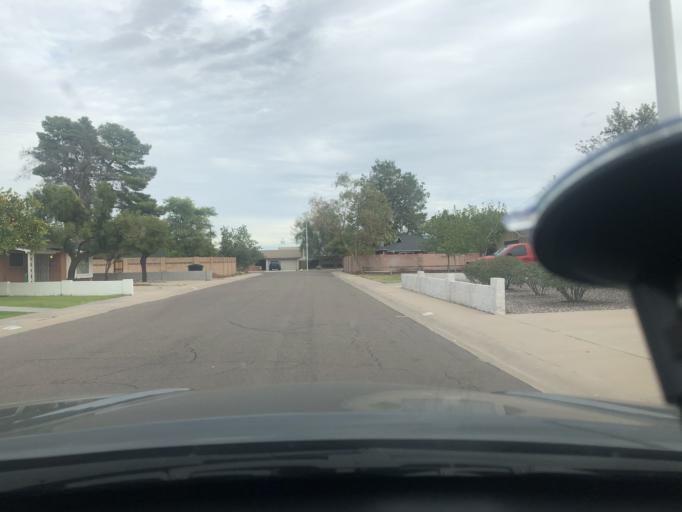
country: US
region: Arizona
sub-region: Maricopa County
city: Scottsdale
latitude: 33.4892
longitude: -111.9040
